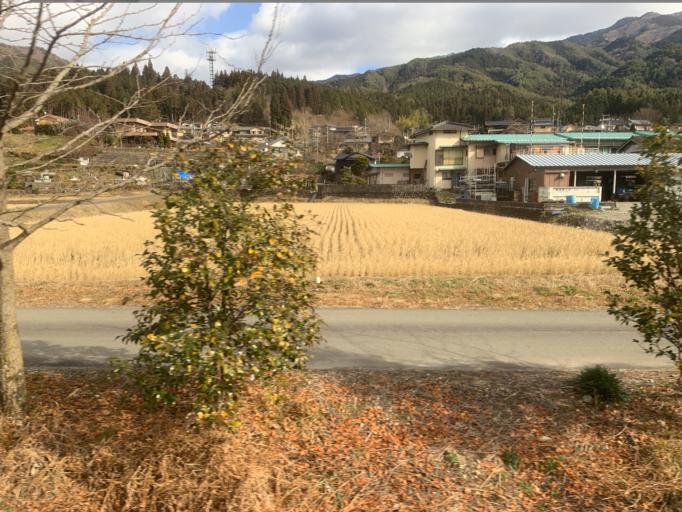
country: JP
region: Gifu
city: Takayama
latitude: 35.8768
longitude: 137.2129
